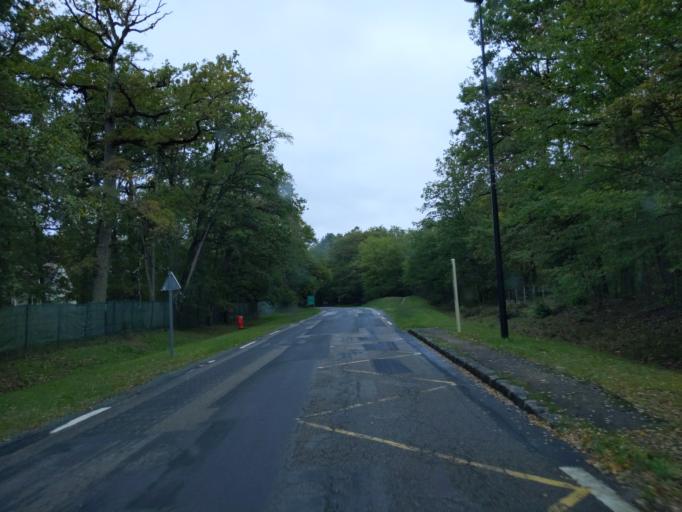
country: FR
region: Ile-de-France
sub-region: Departement des Yvelines
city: Bullion
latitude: 48.5910
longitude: 1.9914
